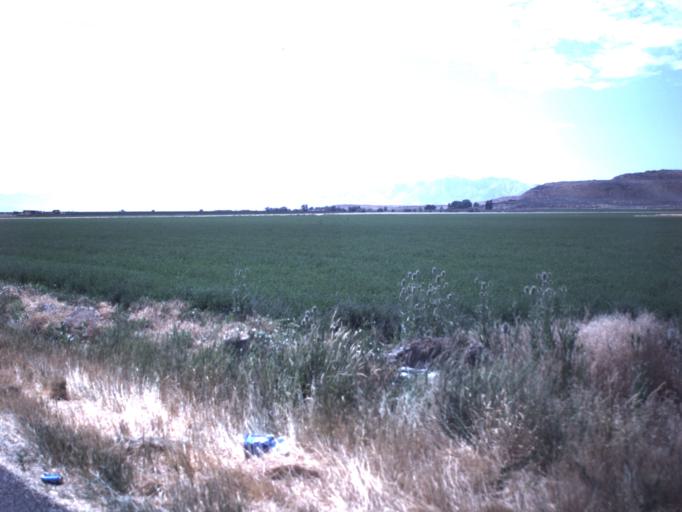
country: US
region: Utah
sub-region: Box Elder County
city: Tremonton
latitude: 41.6485
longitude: -112.3143
